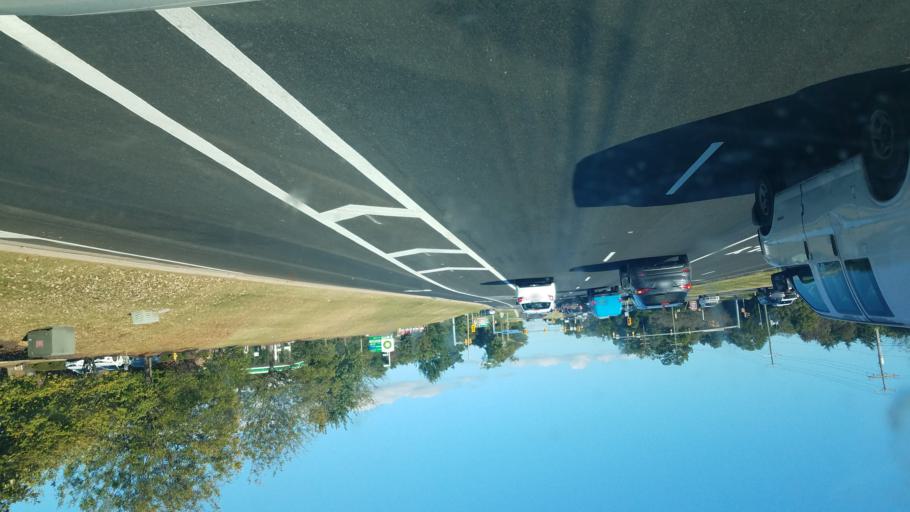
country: US
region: Virginia
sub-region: Prince William County
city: Gainesville
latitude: 38.7919
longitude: -77.6286
